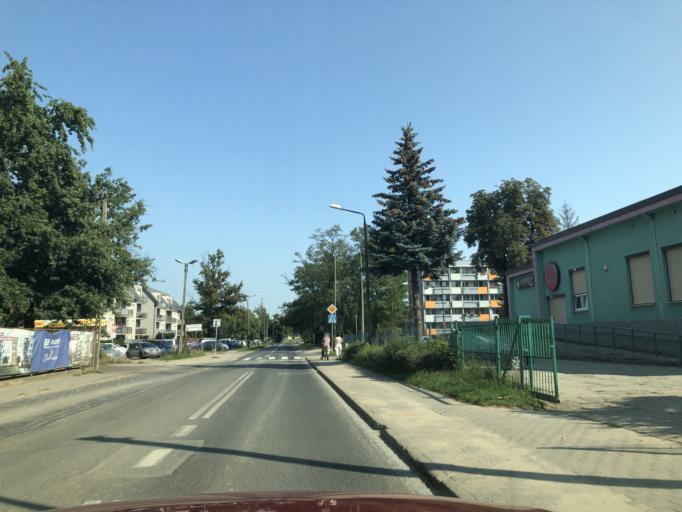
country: PL
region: Lower Silesian Voivodeship
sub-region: Powiat wroclawski
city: Smolec
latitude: 51.1666
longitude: 16.8986
